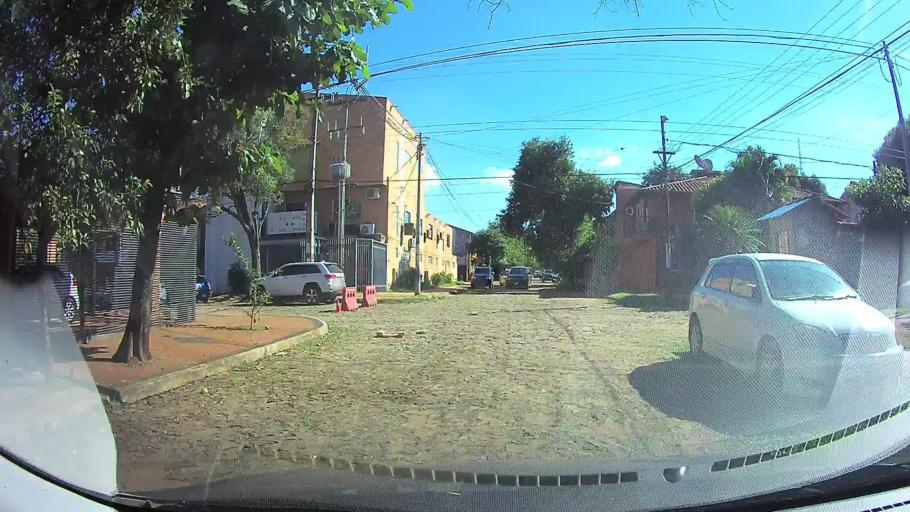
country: PY
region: Central
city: Fernando de la Mora
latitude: -25.3113
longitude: -57.5623
